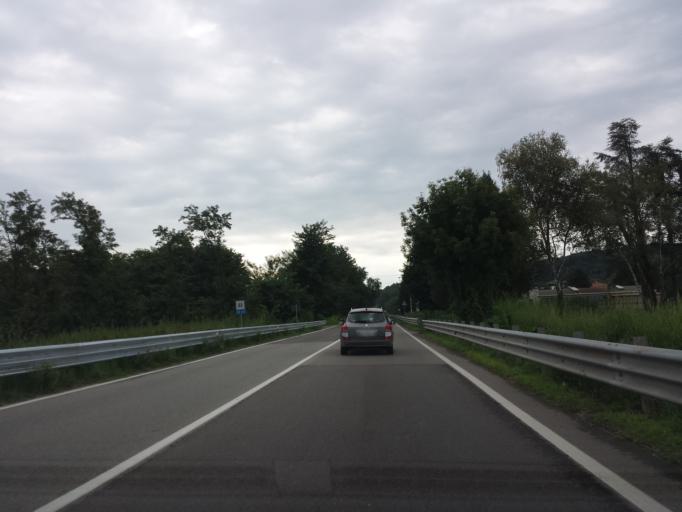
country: IT
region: Lombardy
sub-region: Provincia di Varese
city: Golasecca
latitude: 45.7225
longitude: 8.6619
